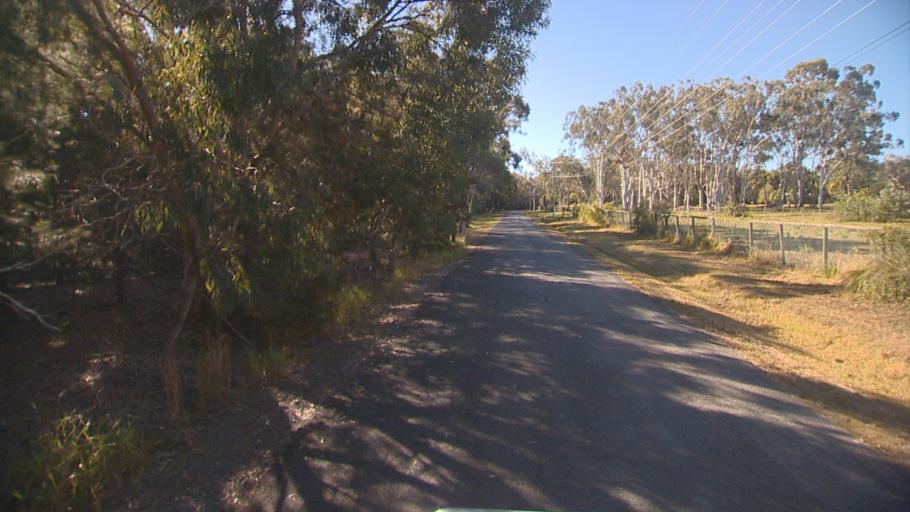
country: AU
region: Queensland
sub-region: Logan
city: Logan Reserve
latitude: -27.7307
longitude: 153.0830
